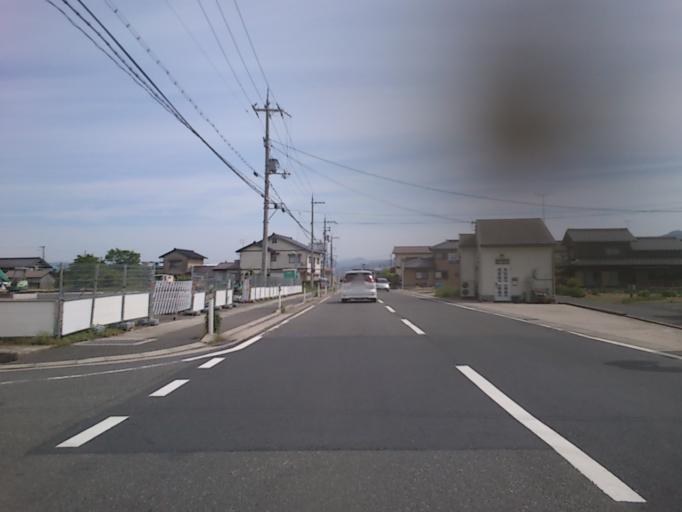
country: JP
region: Kyoto
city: Miyazu
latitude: 35.6220
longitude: 135.0741
